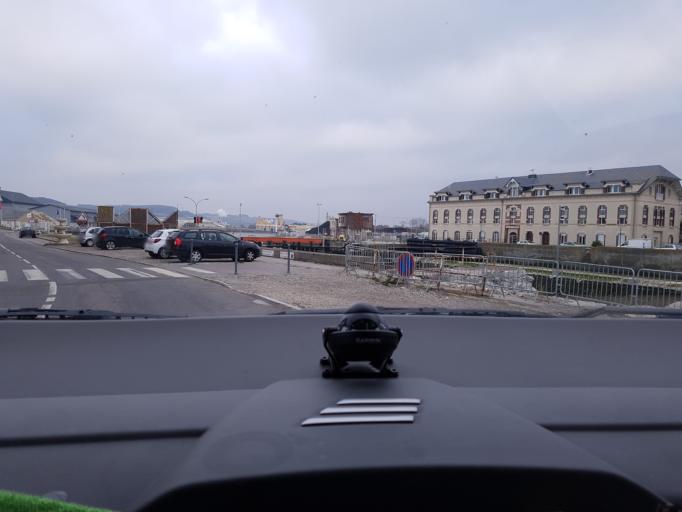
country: FR
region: Haute-Normandie
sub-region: Departement de la Seine-Maritime
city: Le Treport
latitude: 50.0619
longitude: 1.3752
